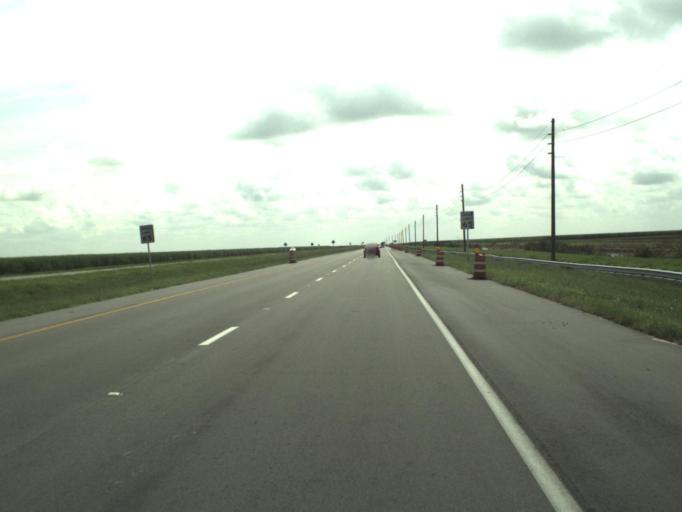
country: US
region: Florida
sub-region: Palm Beach County
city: Belle Glade
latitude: 26.7261
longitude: -80.6493
